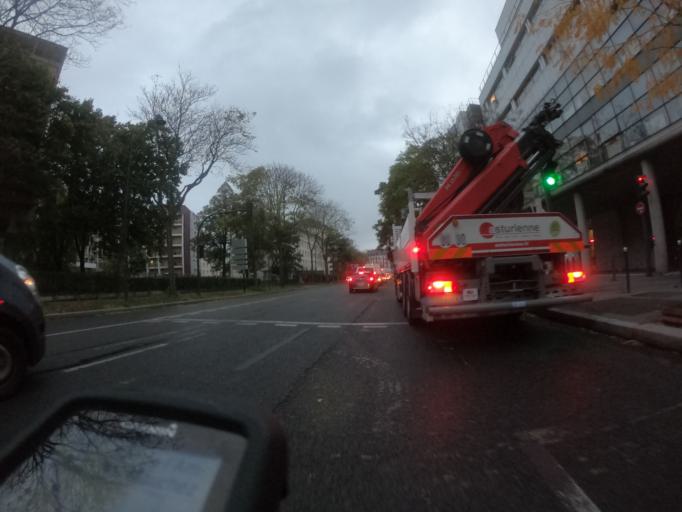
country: FR
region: Ile-de-France
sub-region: Departement du Val-de-Marne
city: Gentilly
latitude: 48.8178
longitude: 2.3442
